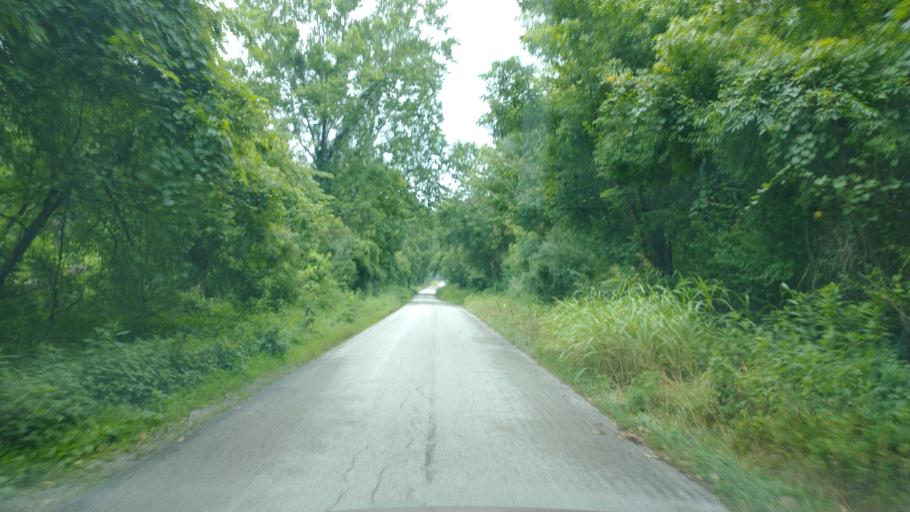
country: US
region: Ohio
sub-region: Meigs County
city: Middleport
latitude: 38.9339
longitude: -82.0816
